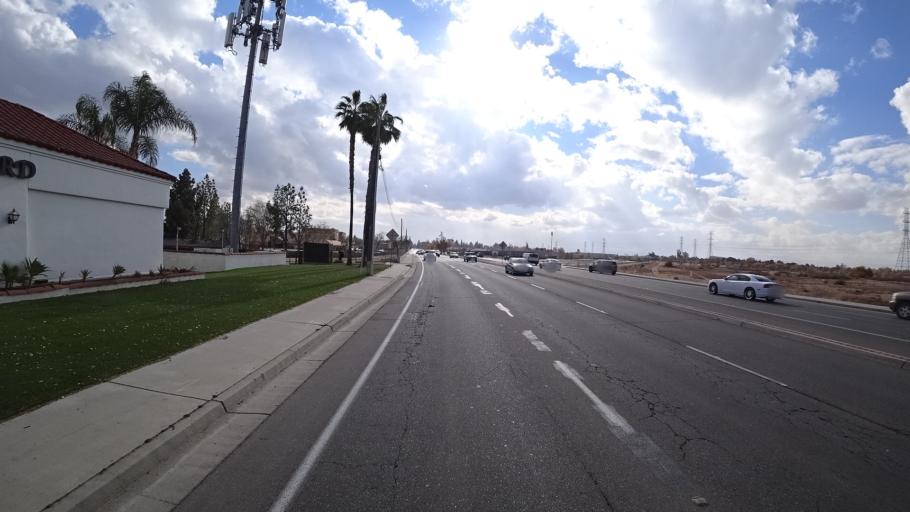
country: US
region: California
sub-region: Kern County
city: Greenacres
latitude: 35.3601
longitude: -119.0921
